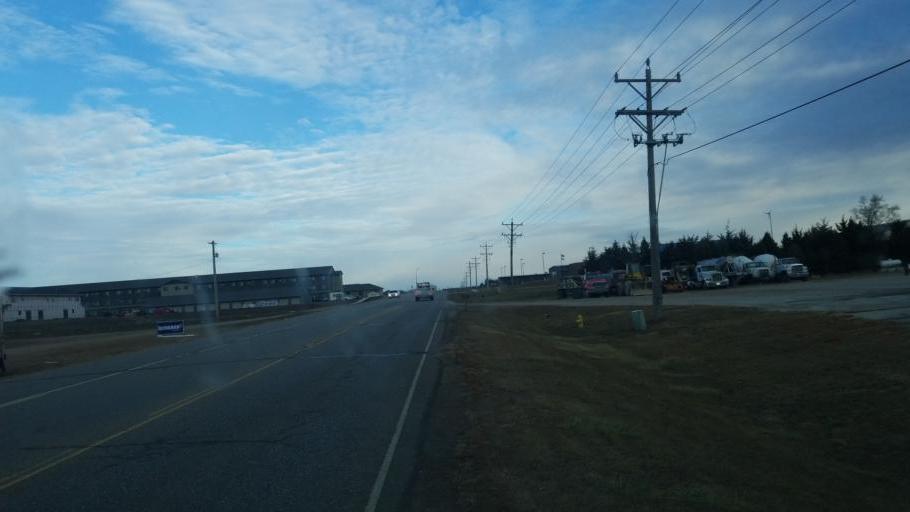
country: US
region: South Dakota
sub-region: Yankton County
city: Yankton
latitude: 42.8950
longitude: -97.4170
